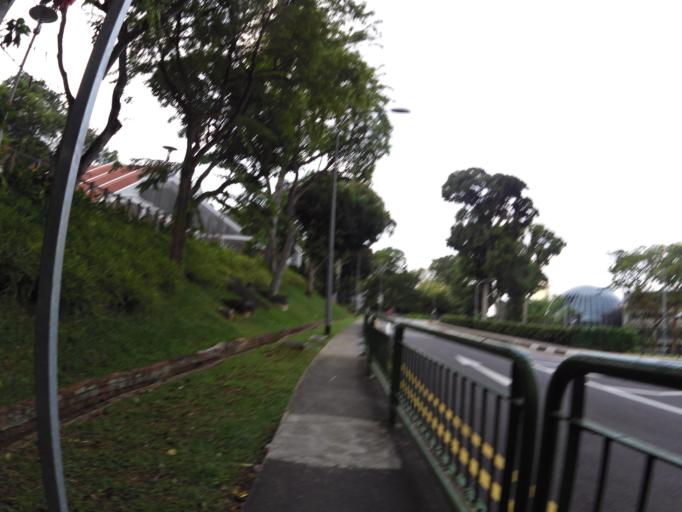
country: SG
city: Singapore
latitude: 1.2939
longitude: 103.8484
